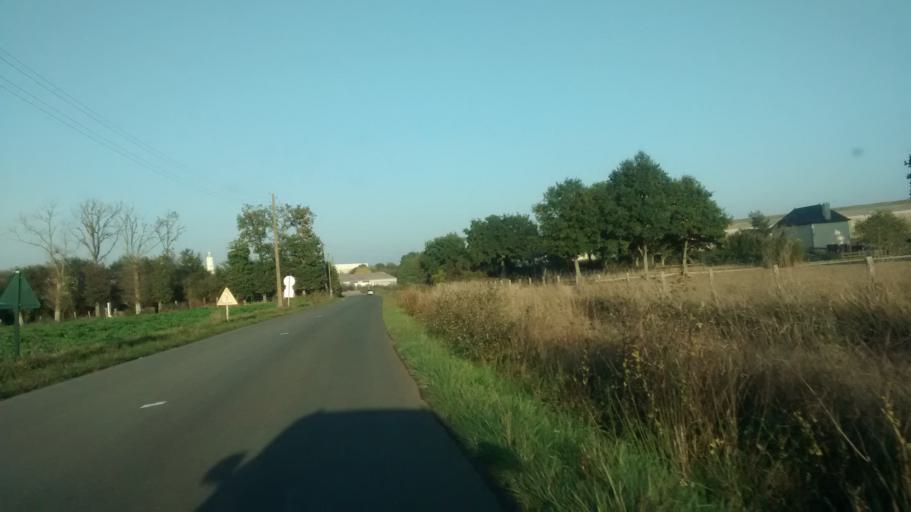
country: FR
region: Brittany
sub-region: Departement d'Ille-et-Vilaine
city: La Chapelle-Thouarault
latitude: 48.1204
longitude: -1.8340
